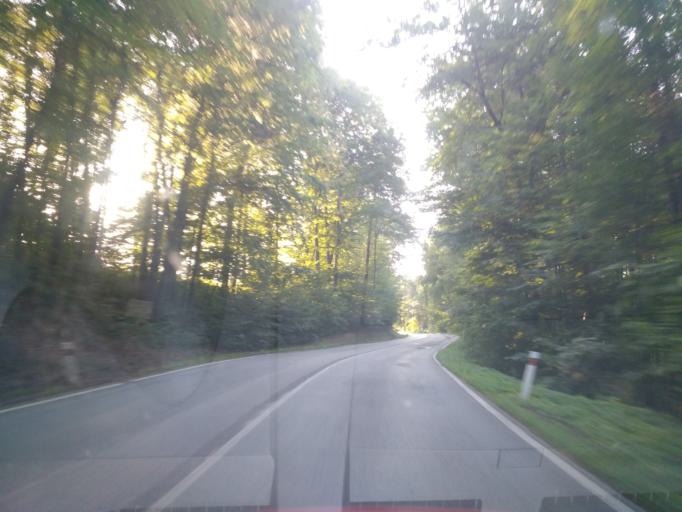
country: SK
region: Presovsky
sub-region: Okres Presov
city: Presov
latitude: 48.9884
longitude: 21.1837
